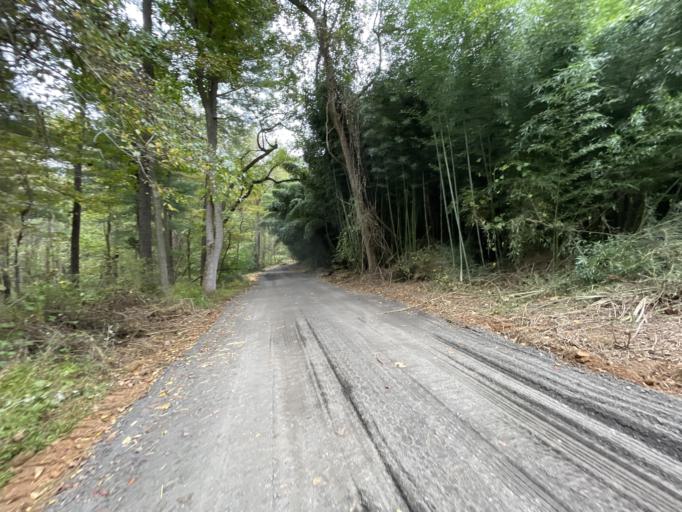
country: US
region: Maryland
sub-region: Baltimore County
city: Hampton
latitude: 39.4289
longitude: -76.5851
